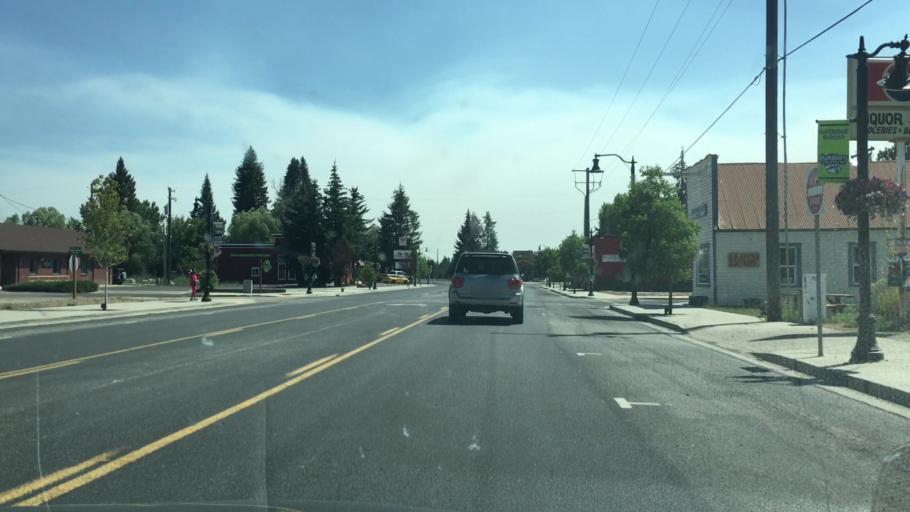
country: US
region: Idaho
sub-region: Valley County
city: McCall
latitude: 44.7324
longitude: -116.0784
